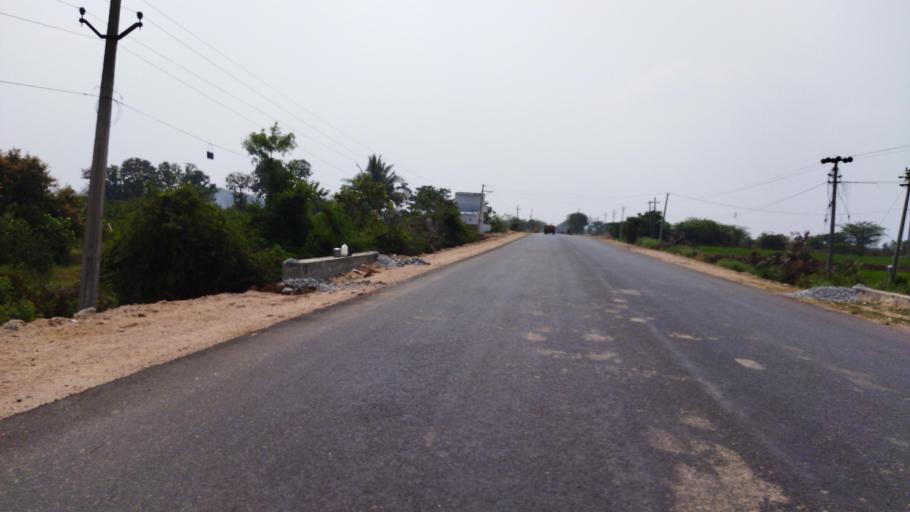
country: IN
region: Telangana
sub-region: Nalgonda
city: Nalgonda
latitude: 17.0855
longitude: 79.3252
